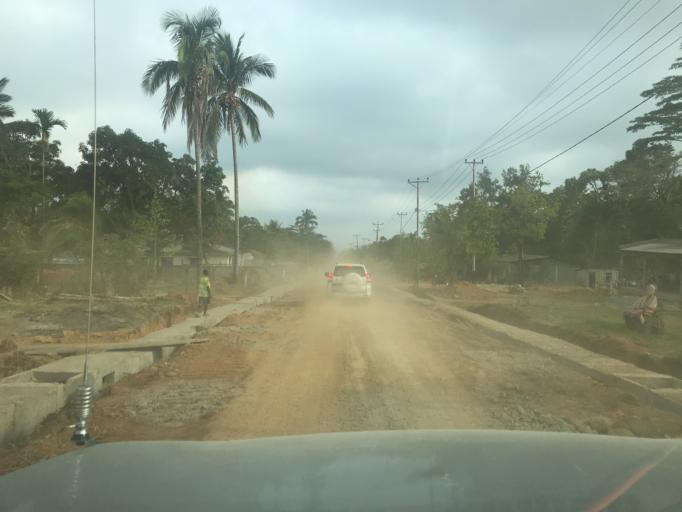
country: TL
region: Ainaro
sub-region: Ainaro
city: Ainaro
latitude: -9.0038
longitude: 125.5013
